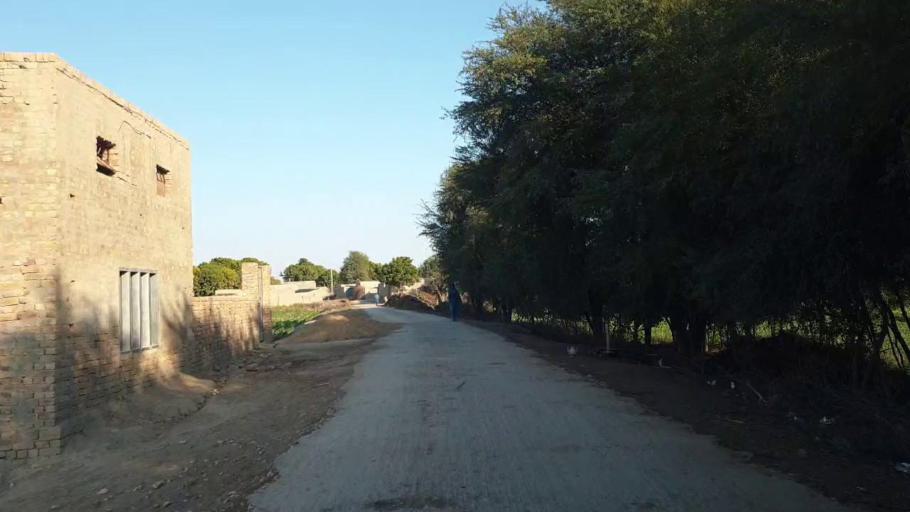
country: PK
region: Sindh
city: Shahpur Chakar
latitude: 26.1285
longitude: 68.5425
